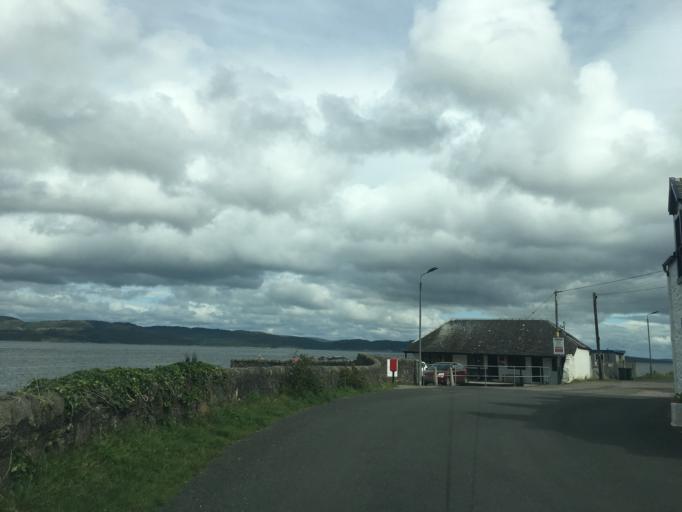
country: GB
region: Scotland
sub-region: Argyll and Bute
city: Tarbert
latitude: 55.8655
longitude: -5.3983
